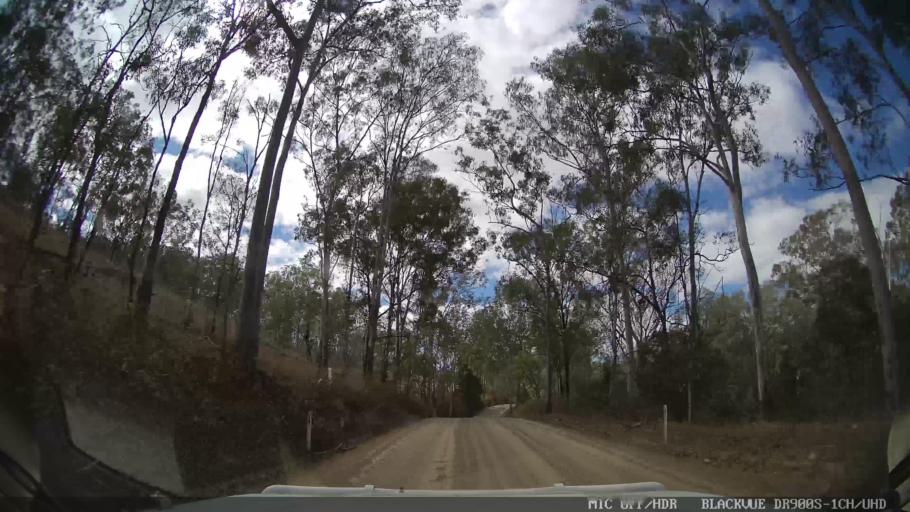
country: AU
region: Queensland
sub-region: Gladstone
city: Toolooa
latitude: -24.5523
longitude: 151.3367
